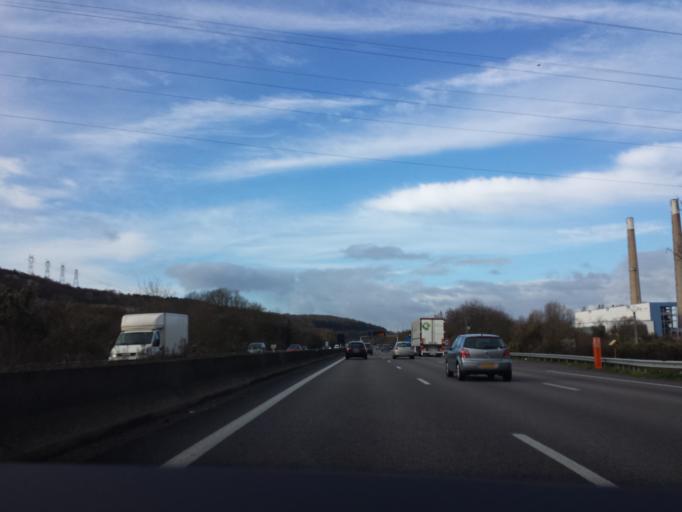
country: FR
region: Ile-de-France
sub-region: Departement des Yvelines
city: Porcheville
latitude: 48.9643
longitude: 1.7715
